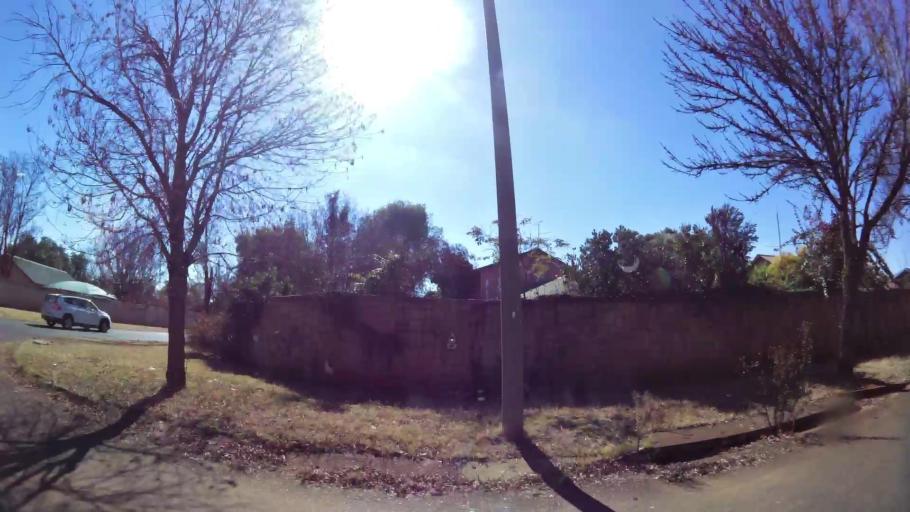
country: ZA
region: Gauteng
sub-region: West Rand District Municipality
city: Carletonville
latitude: -26.3519
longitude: 27.3849
